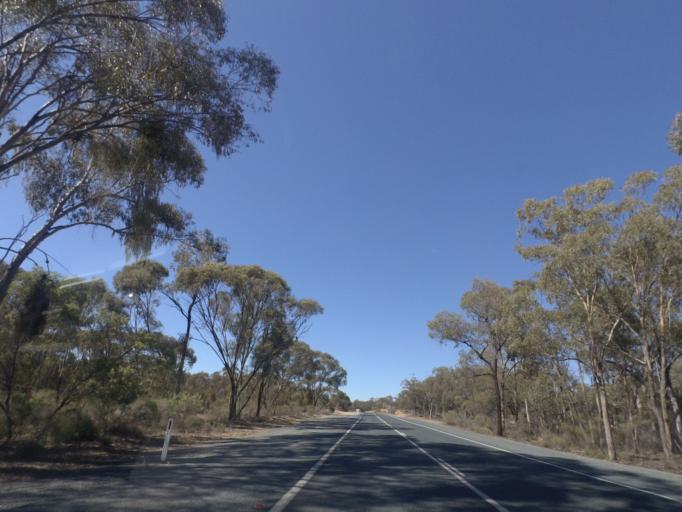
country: AU
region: New South Wales
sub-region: Bland
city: West Wyalong
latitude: -34.1367
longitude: 147.1214
